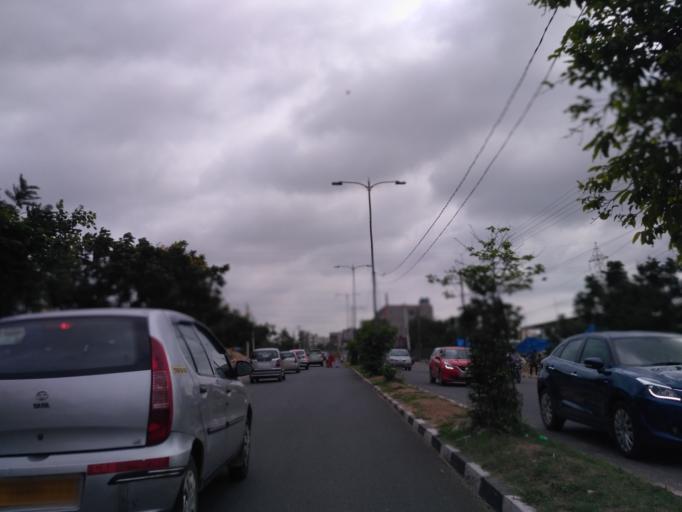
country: IN
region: Telangana
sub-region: Rangareddi
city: Kukatpalli
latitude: 17.4504
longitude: 78.3962
